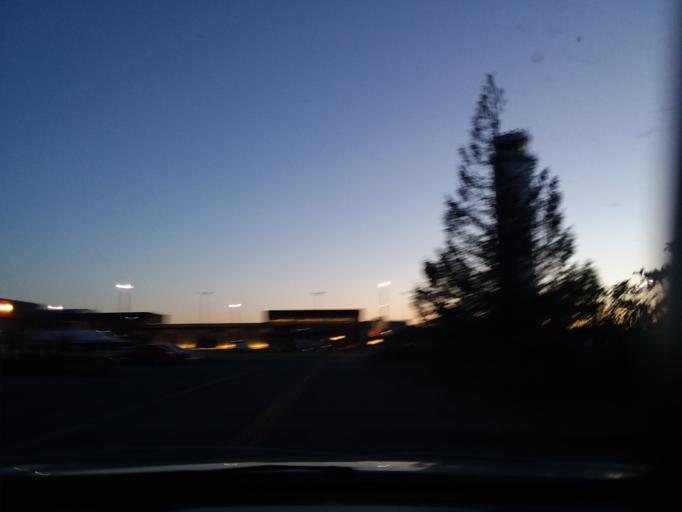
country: US
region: Washington
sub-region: Snohomish County
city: Mukilteo
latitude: 47.9098
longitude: -122.2772
